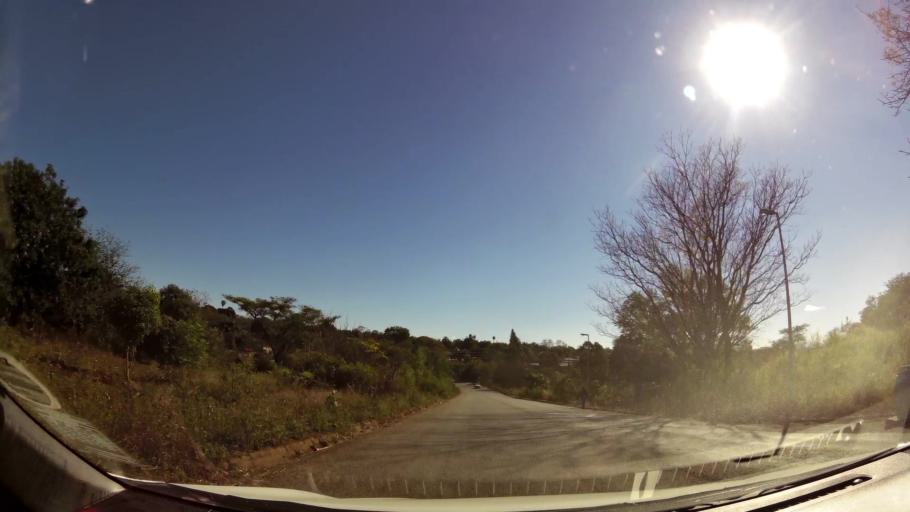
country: ZA
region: Limpopo
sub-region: Mopani District Municipality
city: Tzaneen
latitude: -23.8410
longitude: 30.1668
